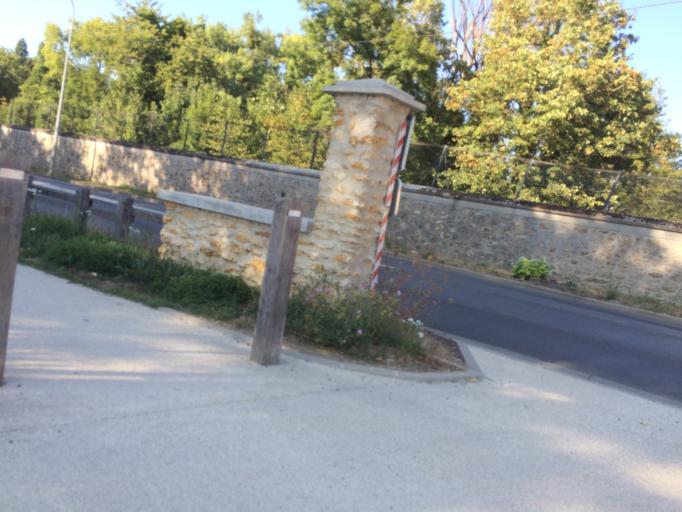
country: FR
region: Ile-de-France
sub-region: Departement de l'Essonne
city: Villiers-sur-Orge
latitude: 48.6562
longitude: 2.3105
